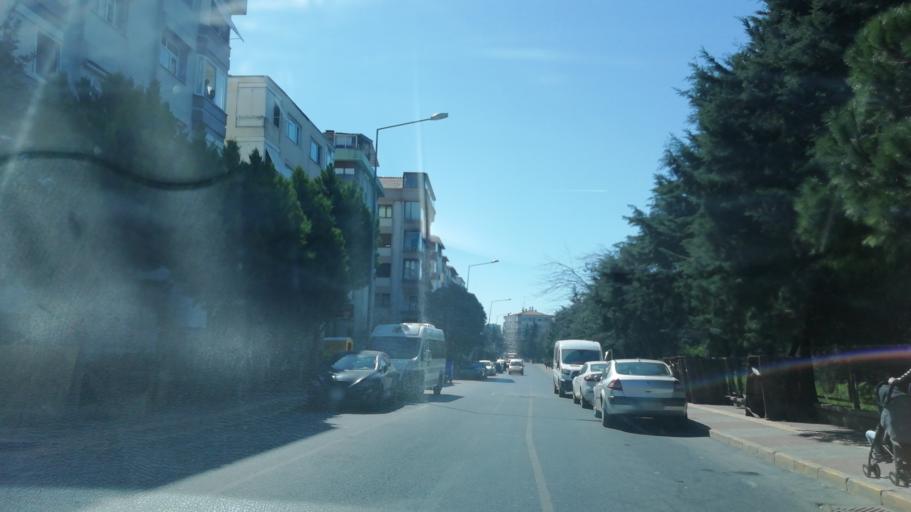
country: TR
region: Istanbul
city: Bahcelievler
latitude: 40.9900
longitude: 28.8667
